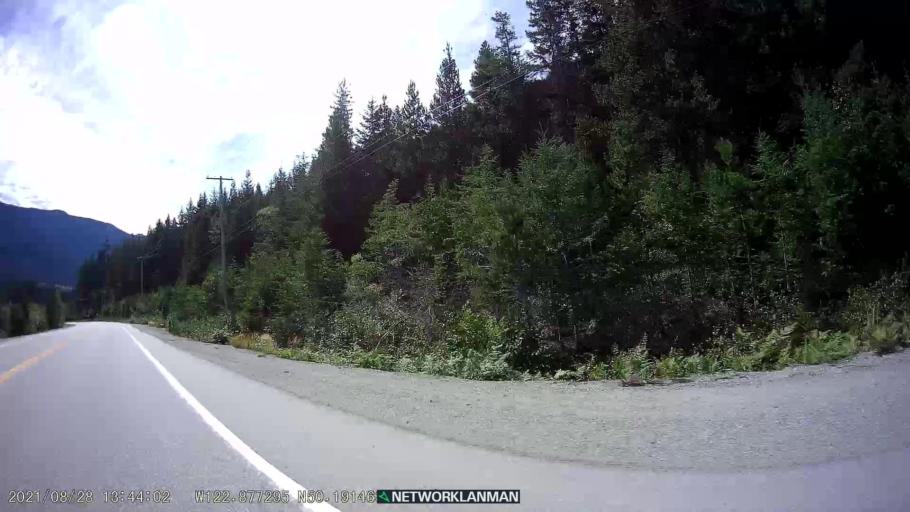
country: CA
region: British Columbia
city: Whistler
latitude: 50.1939
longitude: -122.8797
